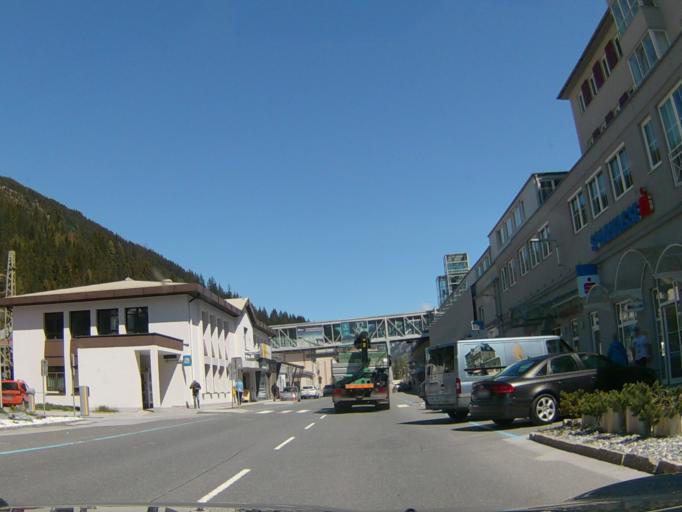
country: AT
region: Salzburg
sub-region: Politischer Bezirk Sankt Johann im Pongau
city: Bad Gastein
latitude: 47.1105
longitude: 13.1328
